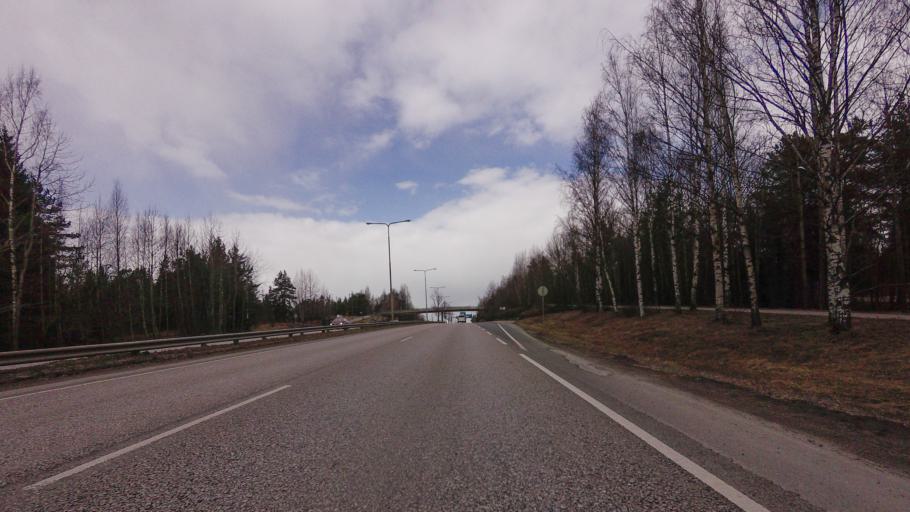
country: FI
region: Uusimaa
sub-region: Helsinki
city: Helsinki
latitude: 60.2318
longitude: 24.9033
